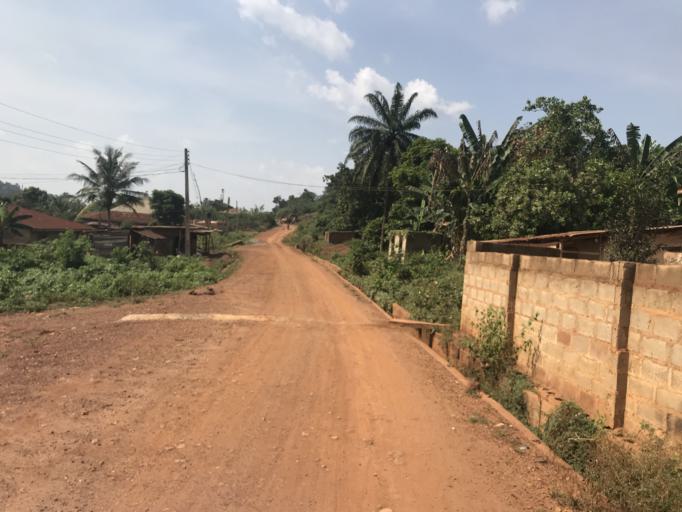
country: NG
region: Osun
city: Ilesa
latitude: 7.6220
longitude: 4.6982
